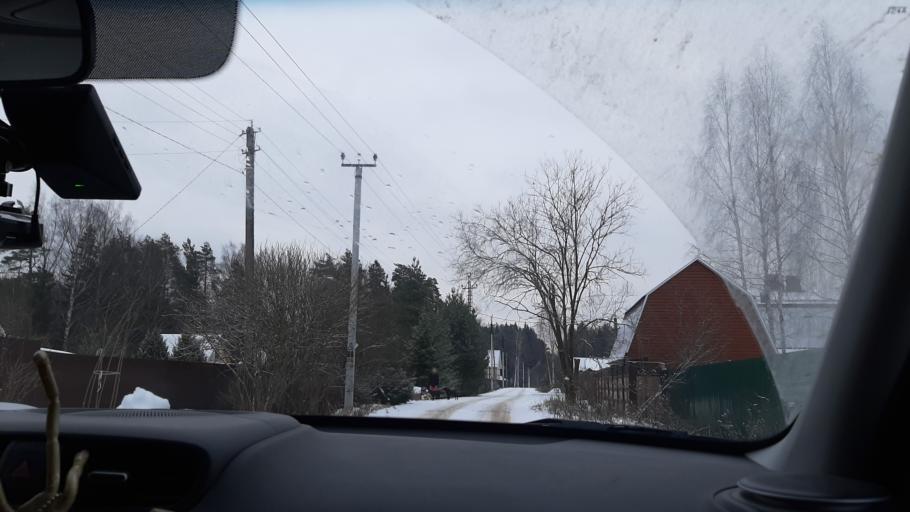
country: RU
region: Ivanovo
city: Kokhma
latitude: 56.9013
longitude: 41.0074
